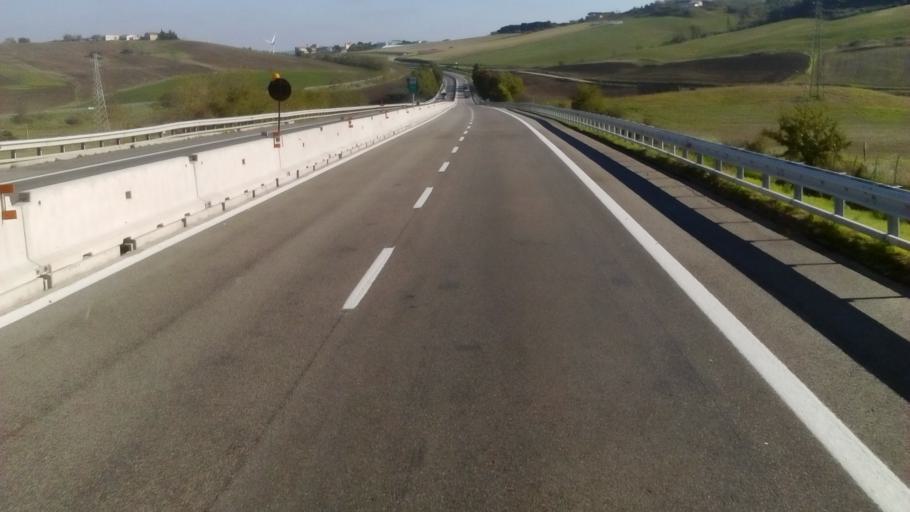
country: IT
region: Apulia
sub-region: Provincia di Foggia
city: Candela
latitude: 41.1492
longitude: 15.5036
